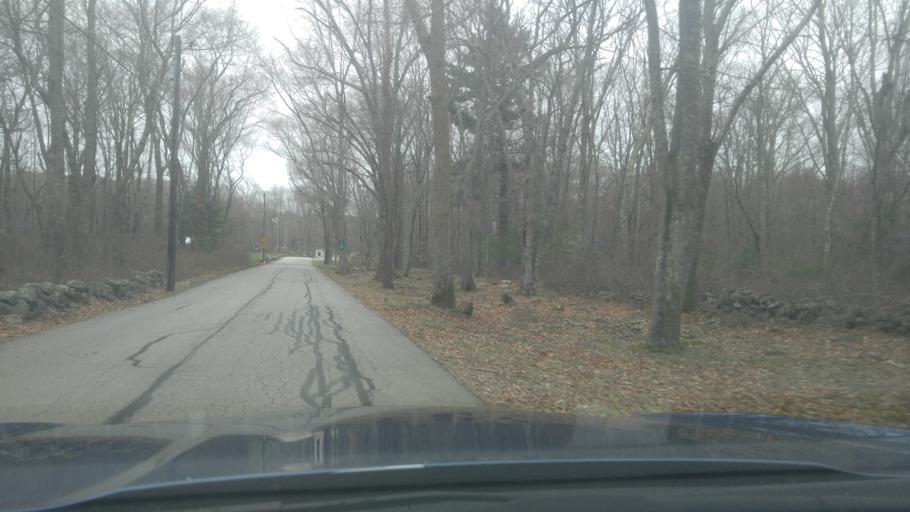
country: US
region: Rhode Island
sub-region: Kent County
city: Coventry
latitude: 41.6812
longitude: -71.6696
